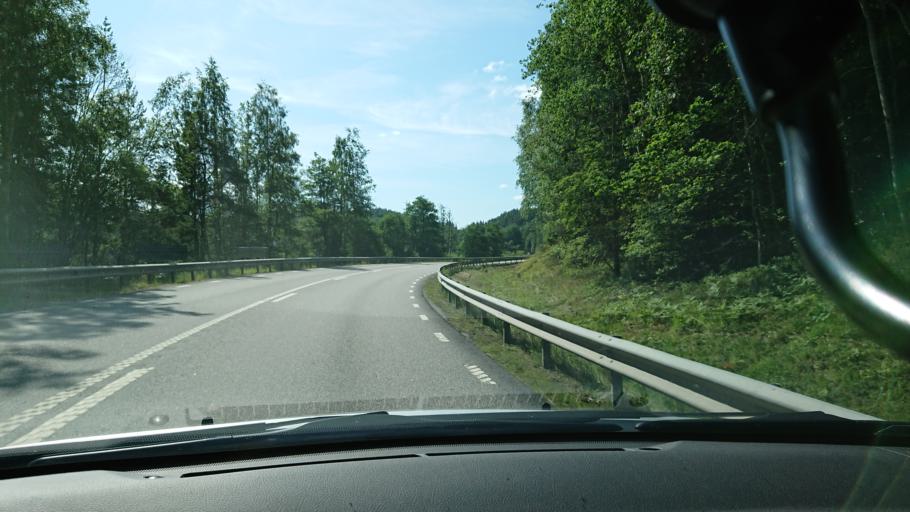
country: SE
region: OEstergoetland
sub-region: Kinda Kommun
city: Kisa
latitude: 57.9591
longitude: 15.6597
